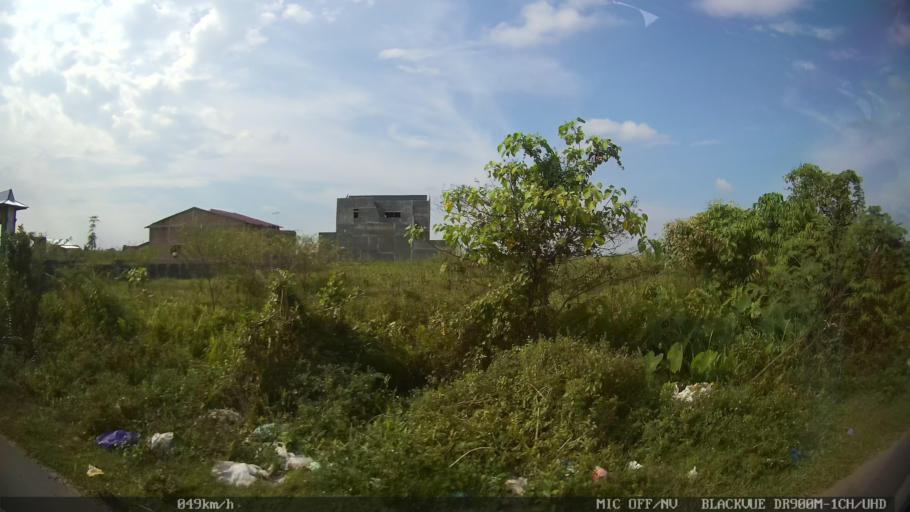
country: ID
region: North Sumatra
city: Medan
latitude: 3.5731
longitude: 98.7645
